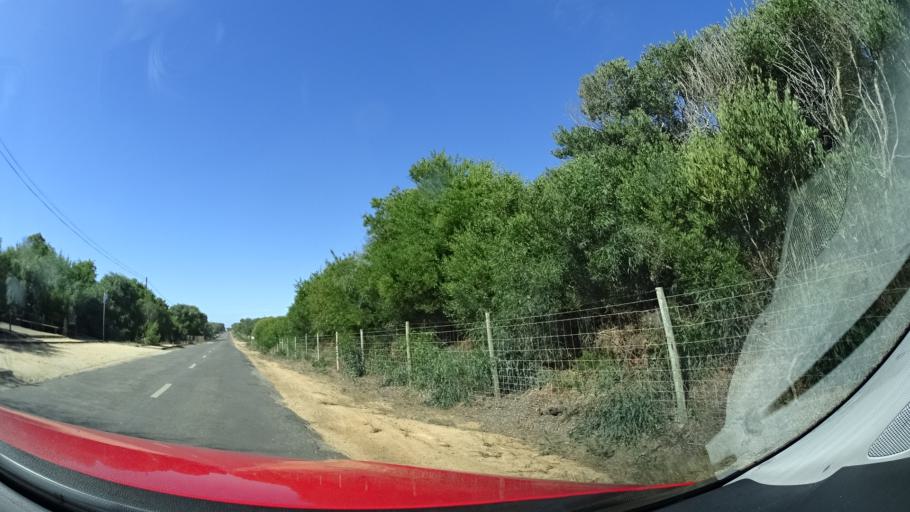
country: PT
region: Beja
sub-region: Odemira
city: Sao Teotonio
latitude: 37.5370
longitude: -8.7852
